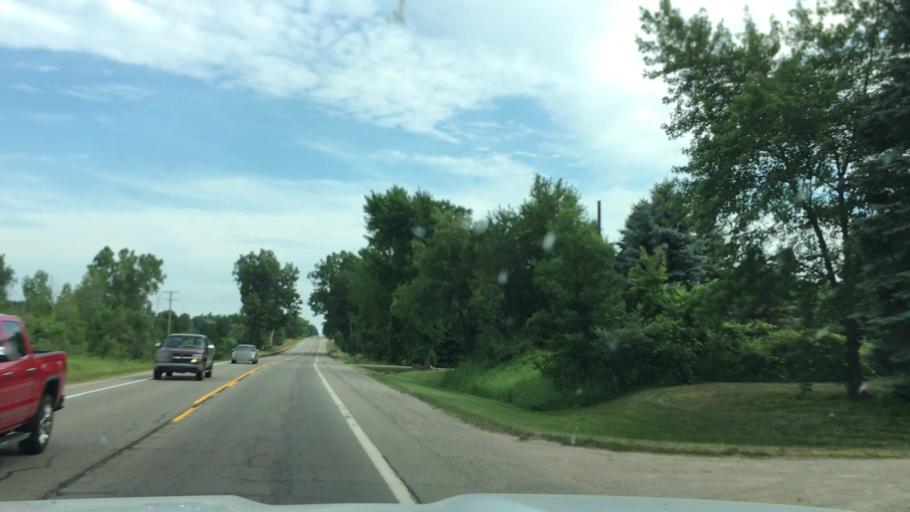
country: US
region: Michigan
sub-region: Sanilac County
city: Brown City
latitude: 43.1468
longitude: -83.0744
